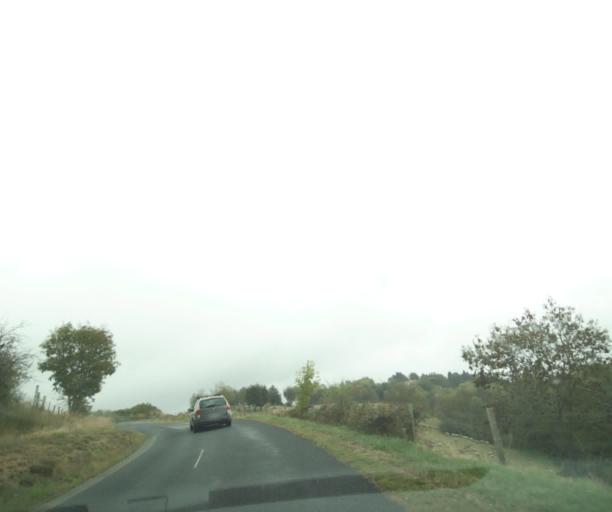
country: FR
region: Auvergne
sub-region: Departement du Puy-de-Dome
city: Saint-Genes-Champanelle
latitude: 45.7215
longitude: 3.0211
